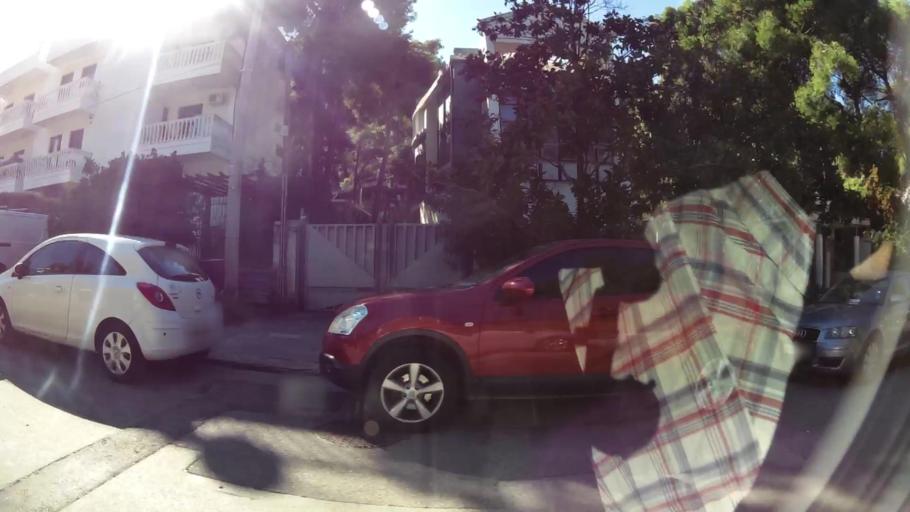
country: GR
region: Attica
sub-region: Nomarchia Athinas
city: Nea Erythraia
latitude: 38.0932
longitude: 23.8001
